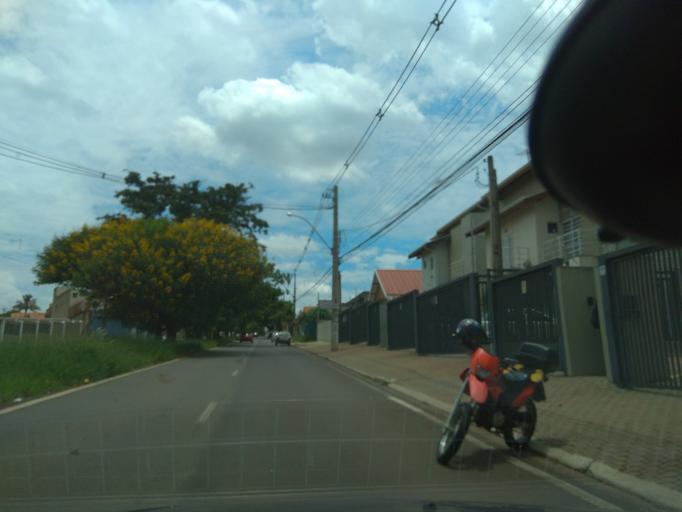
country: BR
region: Sao Paulo
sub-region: Campinas
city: Campinas
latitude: -22.8280
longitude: -47.0739
